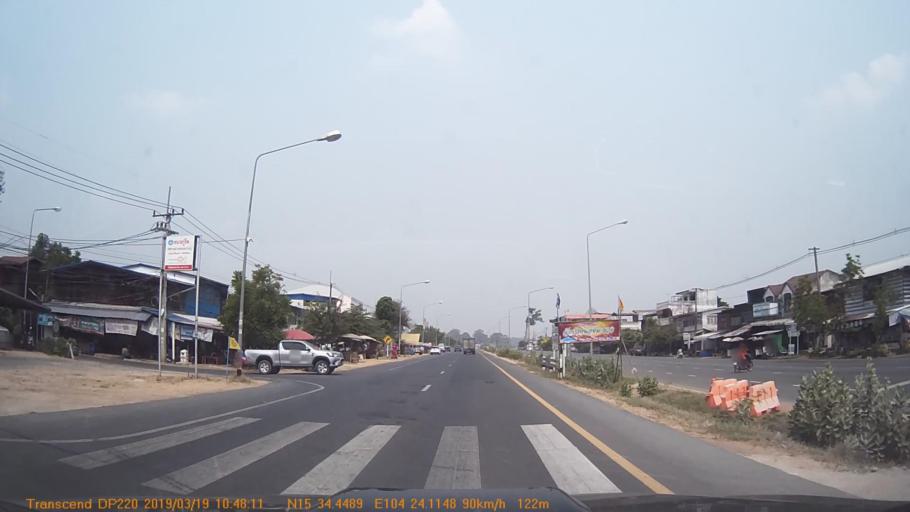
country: TH
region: Yasothon
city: Kham Khuean Kaeo
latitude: 15.5745
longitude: 104.4016
